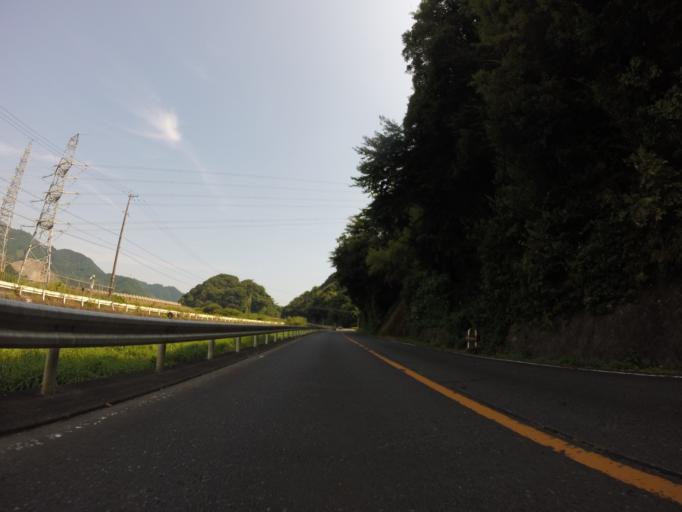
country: JP
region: Shizuoka
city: Shizuoka-shi
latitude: 35.0628
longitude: 138.3601
